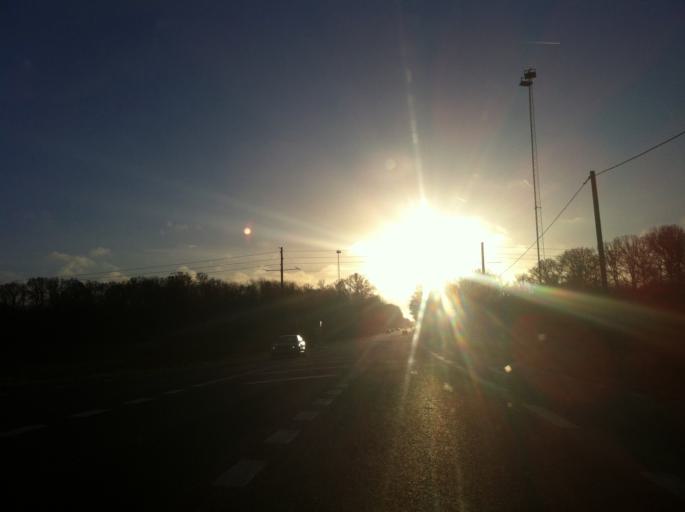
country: SE
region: Skane
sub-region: Hassleholms Kommun
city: Tormestorp
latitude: 56.0855
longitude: 13.7633
